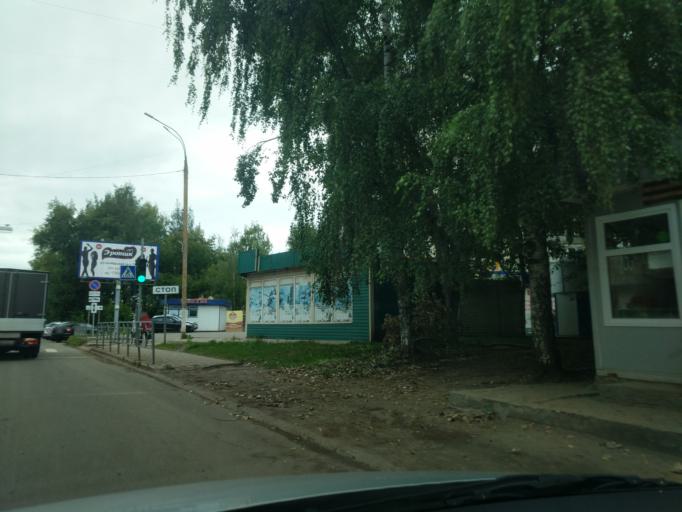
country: RU
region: Kirov
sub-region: Kirovo-Chepetskiy Rayon
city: Kirov
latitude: 58.6333
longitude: 49.6177
